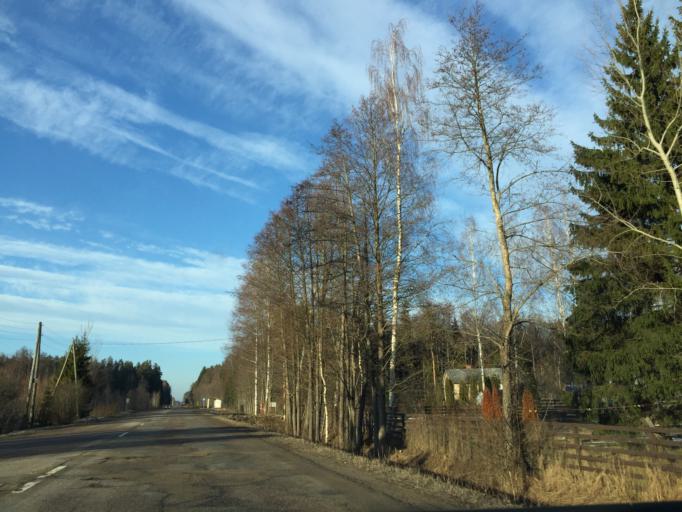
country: LV
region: Lecava
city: Iecava
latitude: 56.7057
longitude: 24.1134
